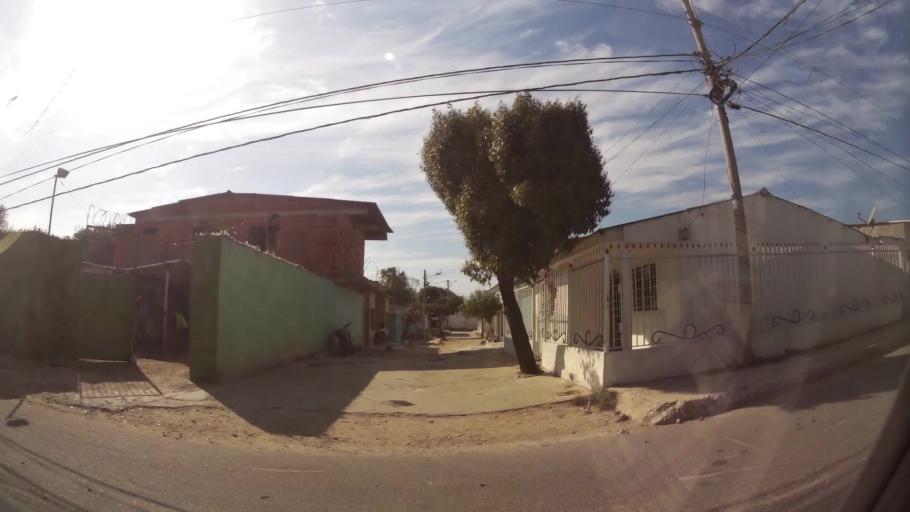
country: CO
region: Atlantico
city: Soledad
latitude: 10.9241
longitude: -74.8165
